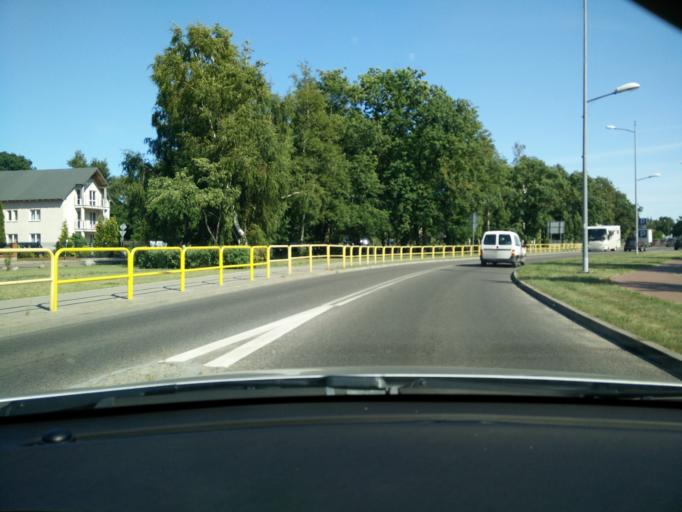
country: PL
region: Pomeranian Voivodeship
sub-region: Powiat pucki
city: Jastarnia
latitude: 54.7059
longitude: 18.6580
